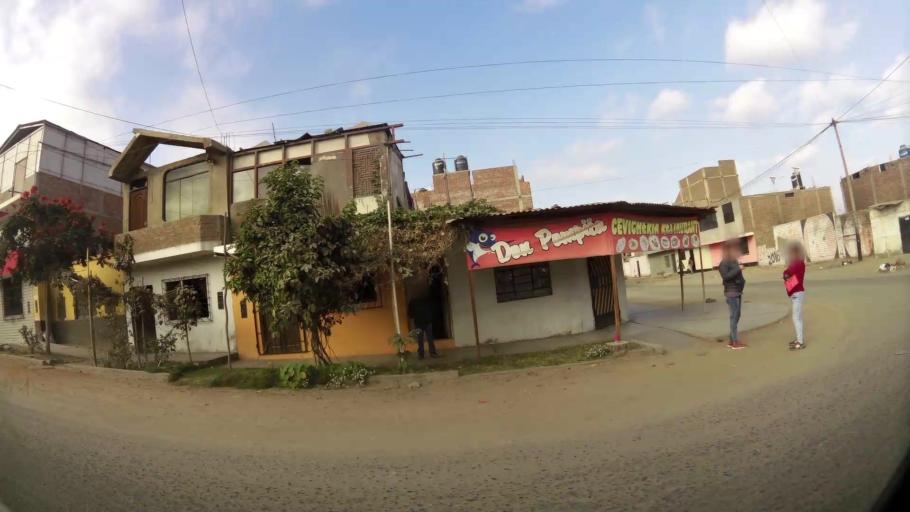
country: PE
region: La Libertad
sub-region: Provincia de Trujillo
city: La Esperanza
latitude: -8.0859
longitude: -79.0338
